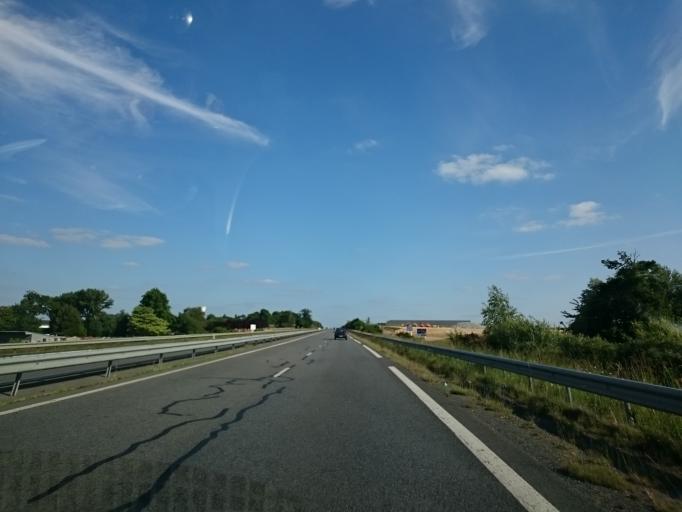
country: FR
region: Brittany
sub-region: Departement d'Ille-et-Vilaine
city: Saint-Armel
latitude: 48.0127
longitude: -1.6009
